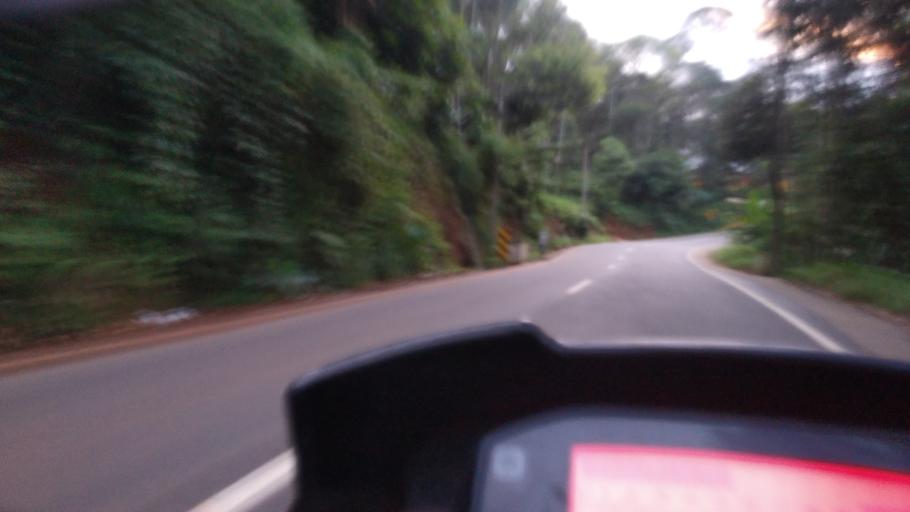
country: IN
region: Kerala
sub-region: Idukki
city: Munnar
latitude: 9.9686
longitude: 77.1201
